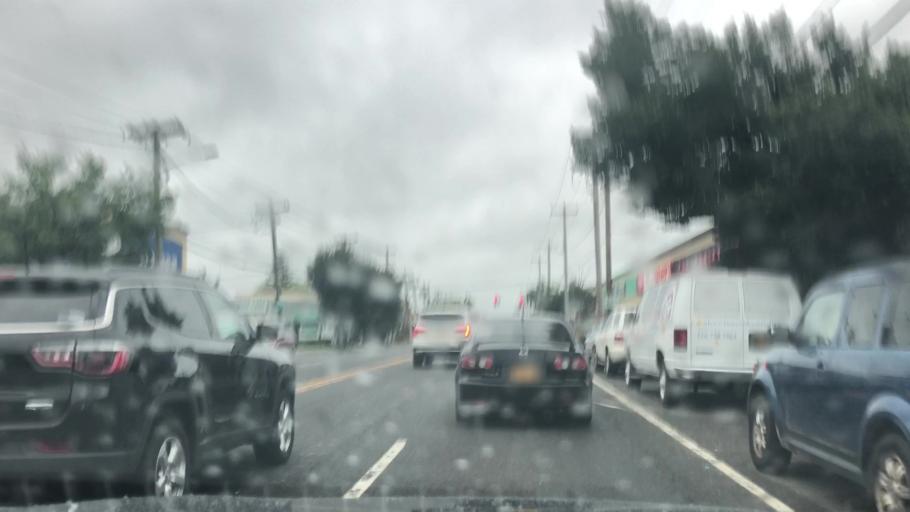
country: US
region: New York
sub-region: Nassau County
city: West Hempstead
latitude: 40.7051
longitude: -73.6450
